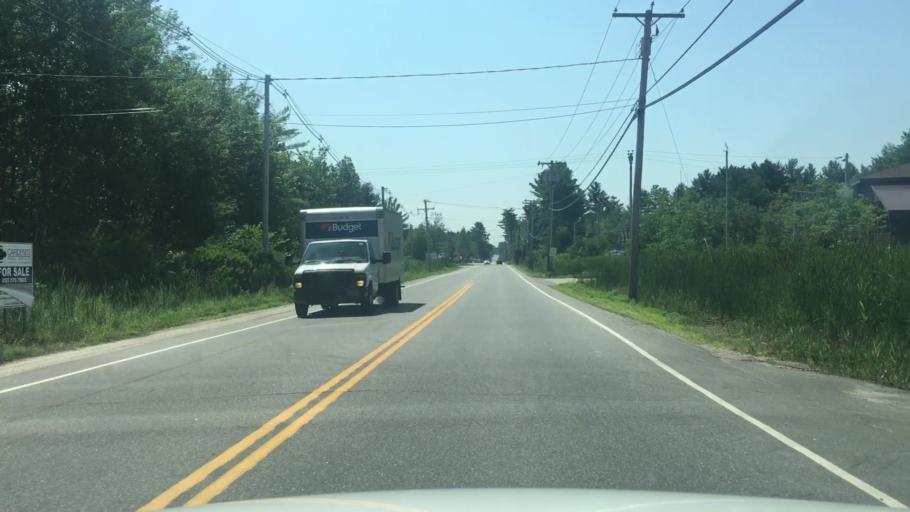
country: US
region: Maine
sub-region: Cumberland County
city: New Gloucester
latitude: 43.8785
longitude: -70.3285
